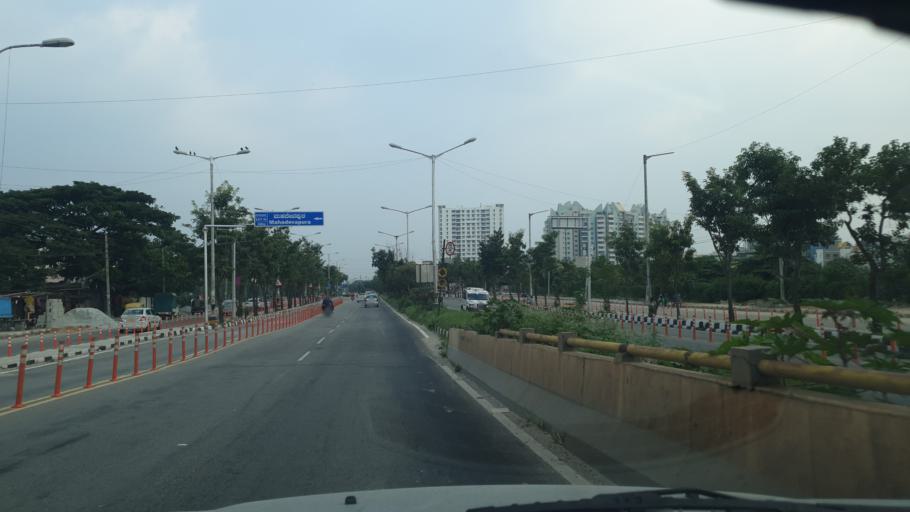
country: IN
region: Karnataka
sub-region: Bangalore Urban
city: Bangalore
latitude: 12.9981
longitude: 77.6825
